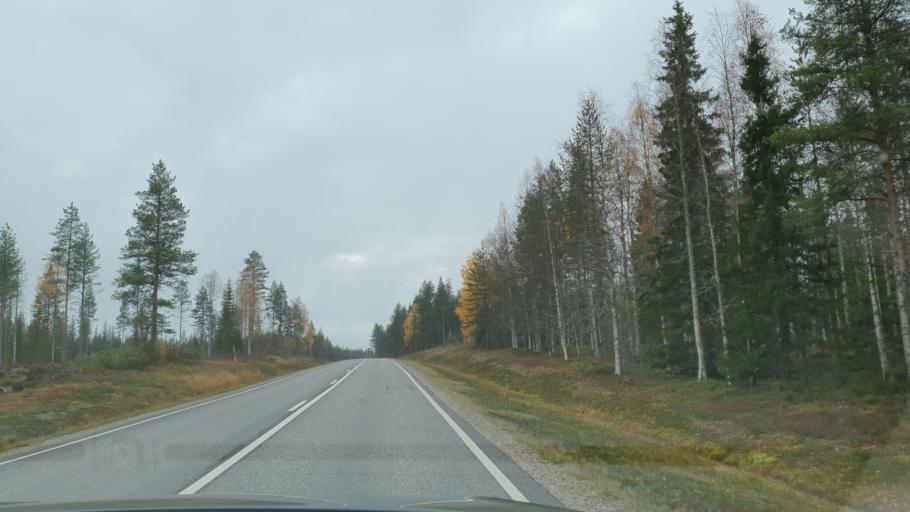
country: FI
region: Lapland
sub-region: Rovaniemi
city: Ranua
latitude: 66.0384
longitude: 26.3392
